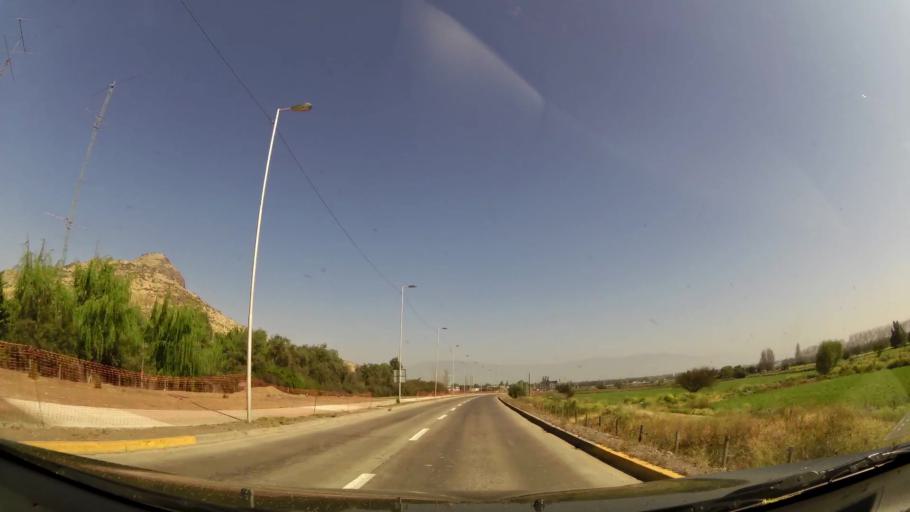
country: CL
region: Santiago Metropolitan
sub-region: Provincia de Chacabuco
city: Chicureo Abajo
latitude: -33.3040
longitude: -70.6786
